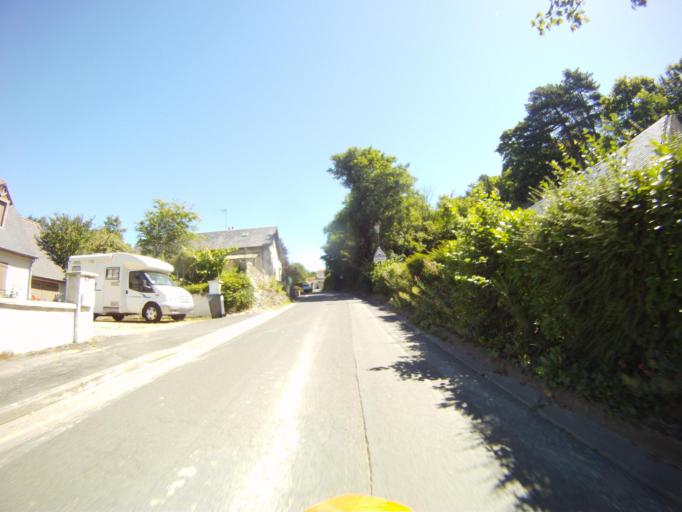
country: FR
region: Centre
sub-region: Departement d'Indre-et-Loire
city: Vouvray
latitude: 47.4369
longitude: 0.7957
